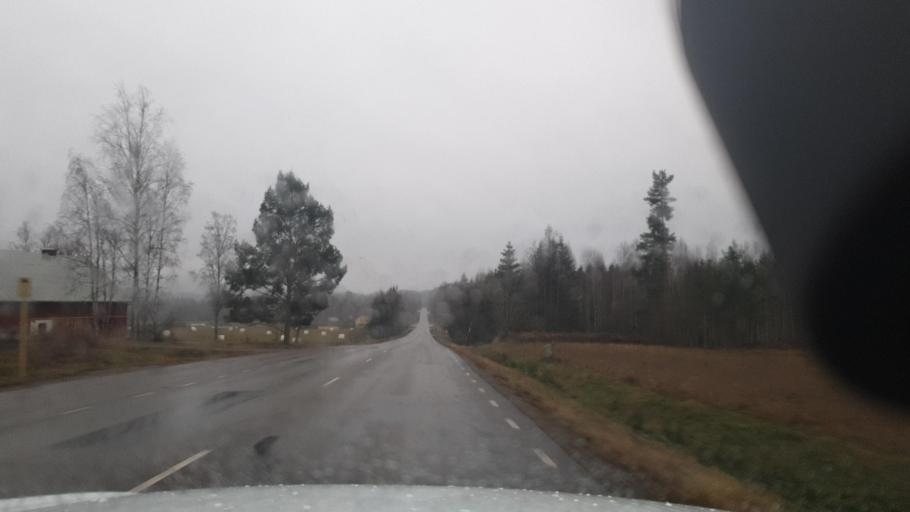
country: SE
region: Vaermland
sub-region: Arvika Kommun
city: Arvika
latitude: 59.6879
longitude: 12.6319
